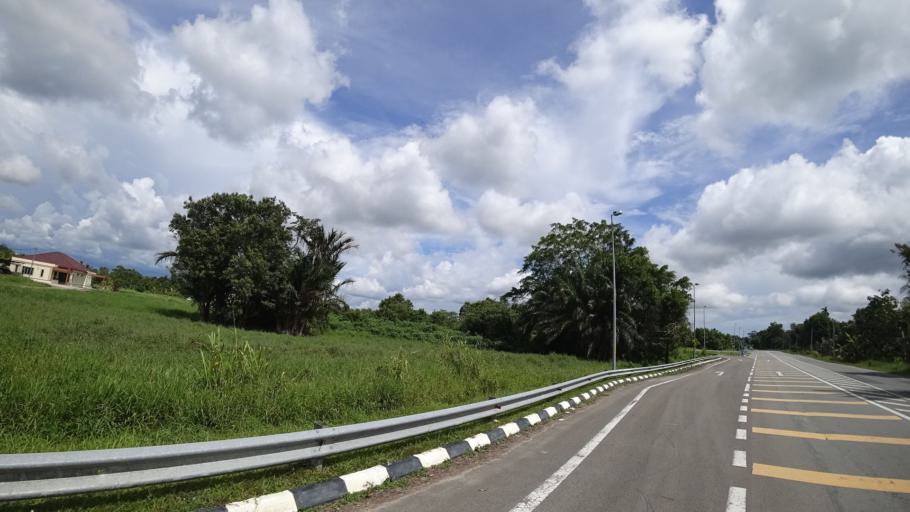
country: BN
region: Tutong
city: Tutong
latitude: 4.7516
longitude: 114.8173
